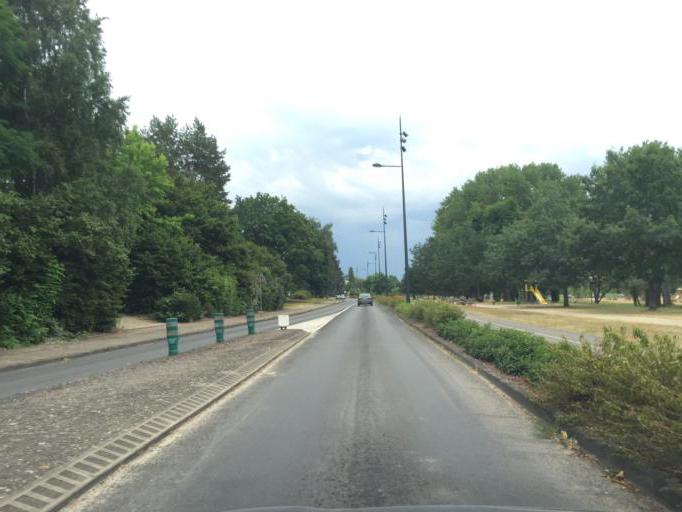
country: FR
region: Auvergne
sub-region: Departement de l'Allier
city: Moulins
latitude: 46.5484
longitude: 3.3320
